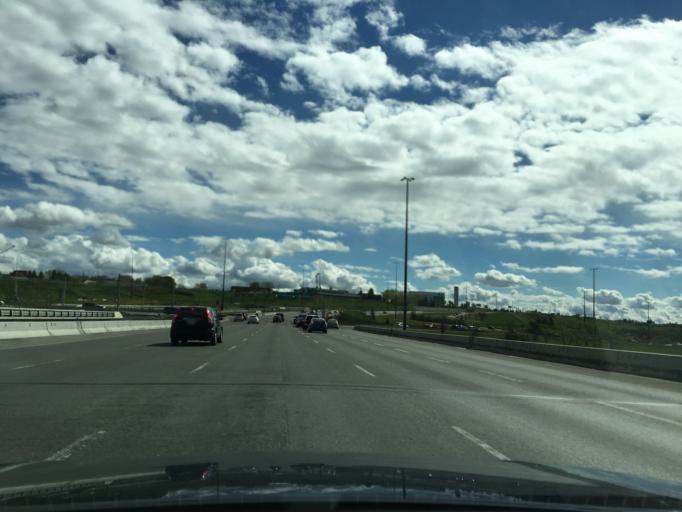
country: CA
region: Alberta
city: Calgary
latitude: 51.0477
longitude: -114.0202
